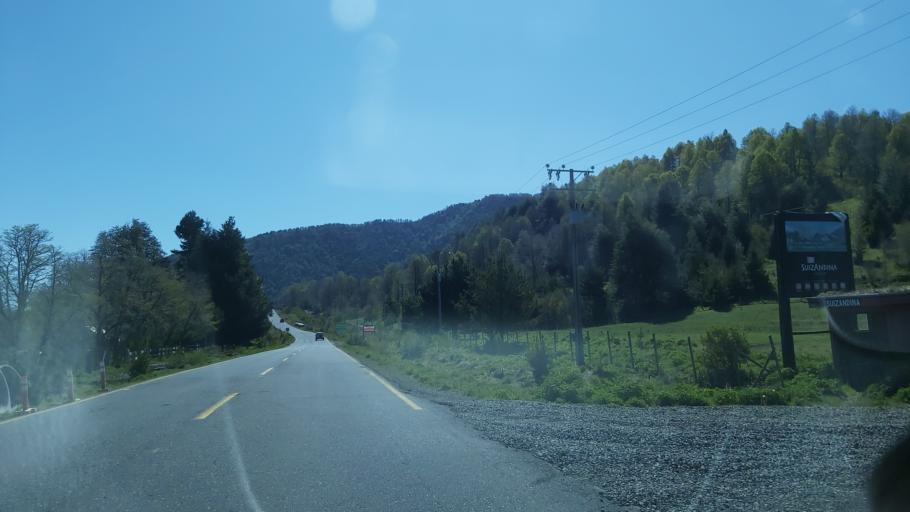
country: CL
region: Araucania
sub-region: Provincia de Cautin
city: Vilcun
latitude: -38.4638
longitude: -71.6159
